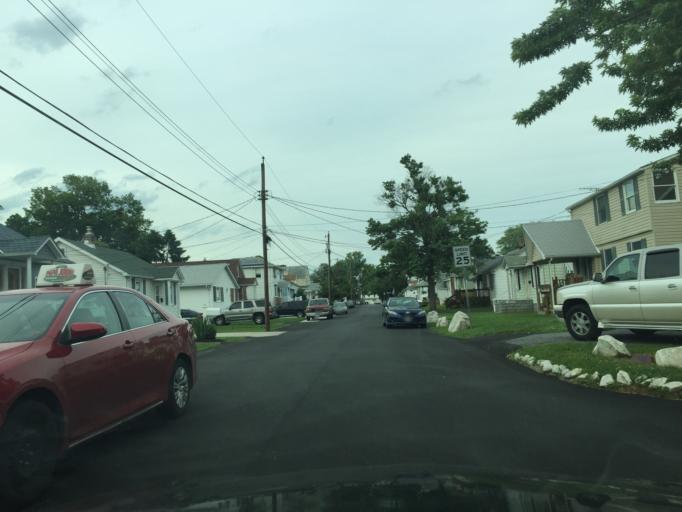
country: US
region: Maryland
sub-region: Baltimore County
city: Middle River
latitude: 39.3301
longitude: -76.4438
